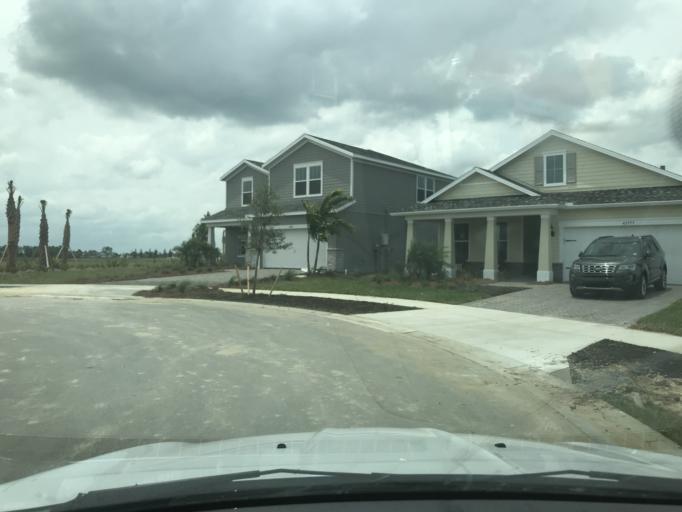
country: US
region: Florida
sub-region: Lee County
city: Olga
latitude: 26.7804
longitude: -81.7444
